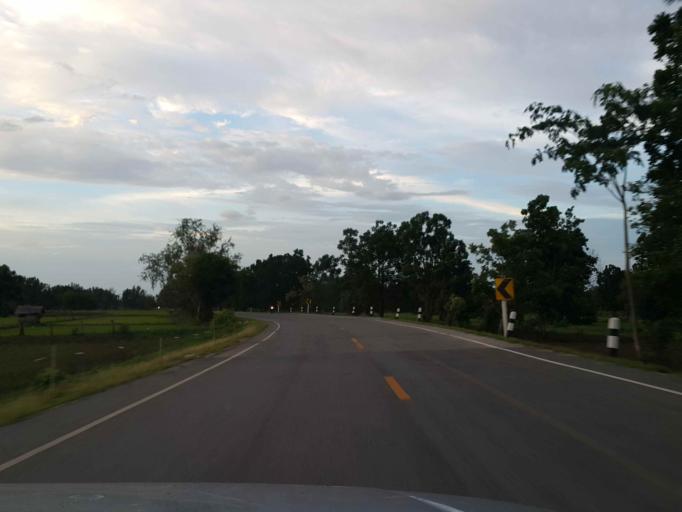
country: TH
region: Sukhothai
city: Ban Dan Lan Hoi
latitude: 17.0810
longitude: 99.5908
